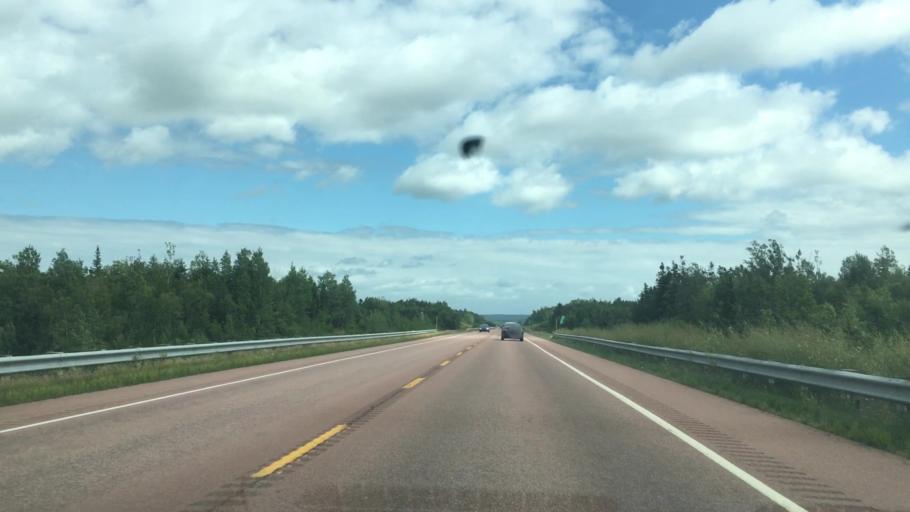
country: CA
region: Nova Scotia
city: Port Hawkesbury
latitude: 45.6082
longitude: -61.6609
